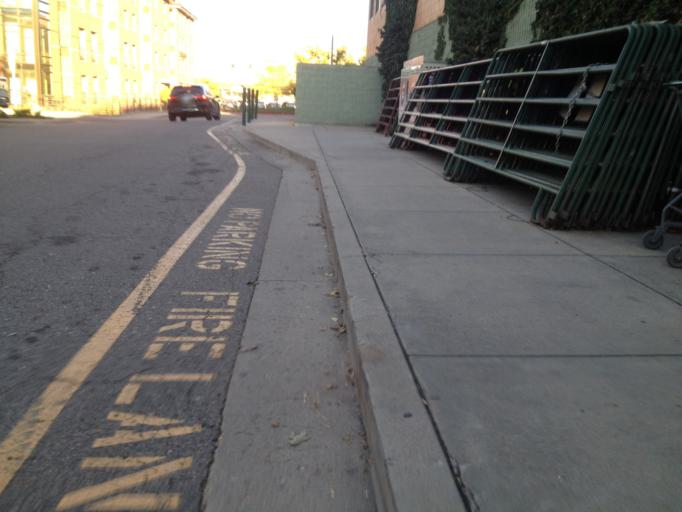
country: US
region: Colorado
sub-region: Boulder County
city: Boulder
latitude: 40.0165
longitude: -105.2619
